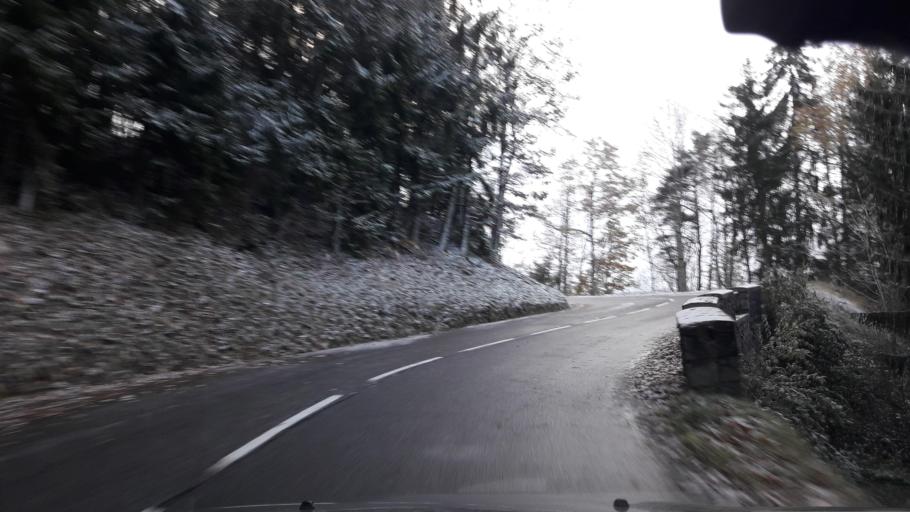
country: FR
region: Rhone-Alpes
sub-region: Departement de l'Isere
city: Allevard
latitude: 45.3848
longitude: 6.0925
